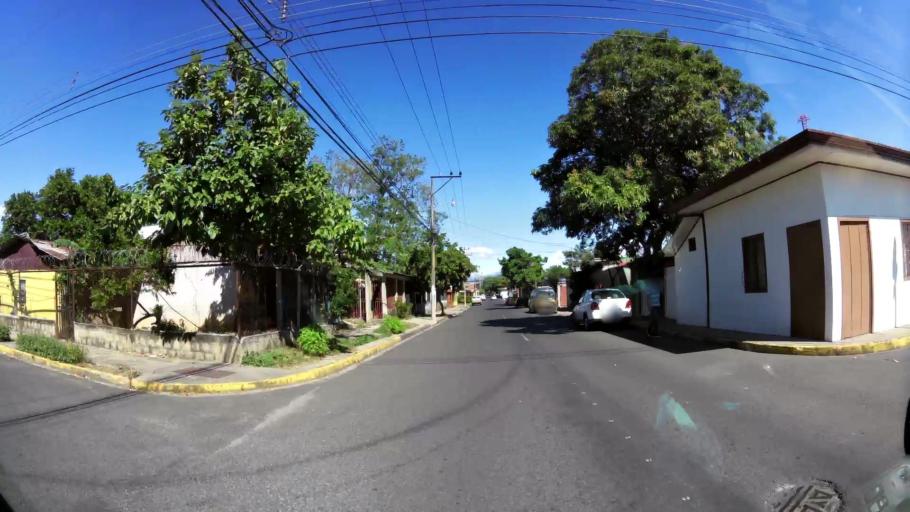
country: CR
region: Guanacaste
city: Liberia
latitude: 10.6333
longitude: -85.4375
